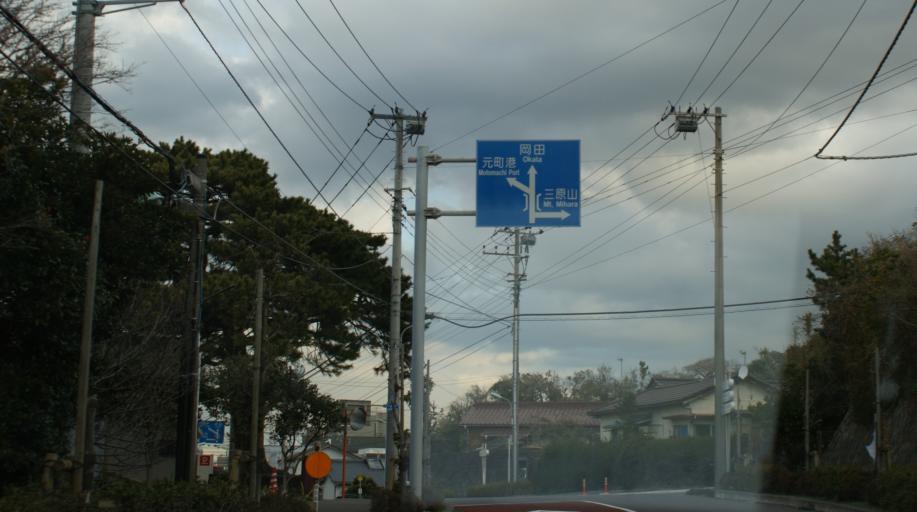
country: JP
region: Shizuoka
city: Ito
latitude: 34.7461
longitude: 139.3569
